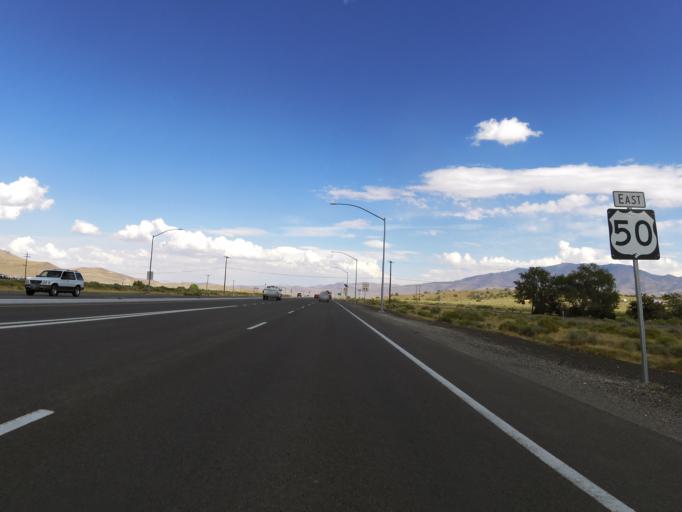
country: US
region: Nevada
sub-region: Lyon County
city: Dayton
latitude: 39.2204
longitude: -119.6464
